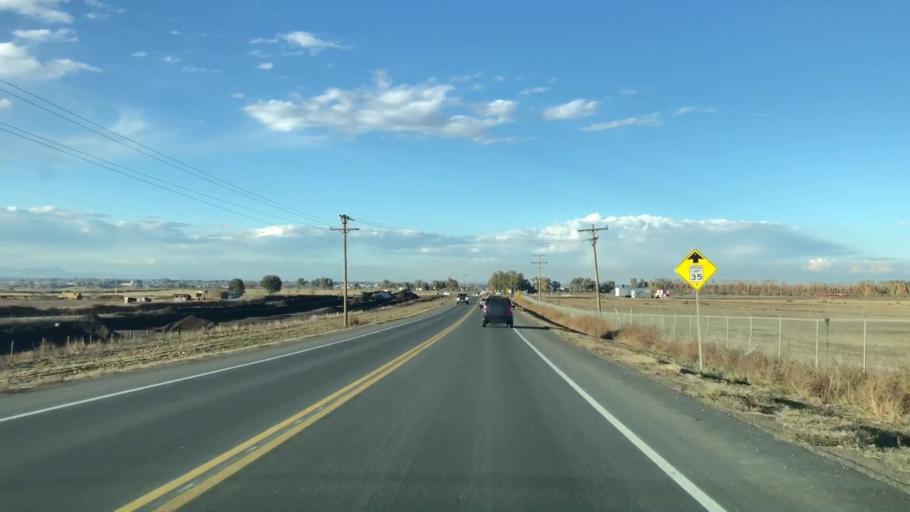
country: US
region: Colorado
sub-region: Larimer County
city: Loveland
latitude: 40.4618
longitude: -105.0204
